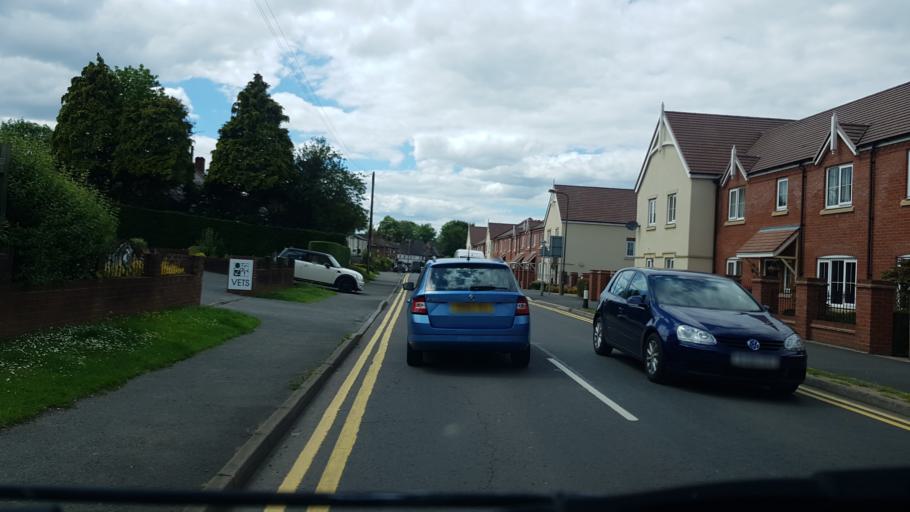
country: GB
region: England
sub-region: Worcestershire
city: Droitwich
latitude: 52.2681
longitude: -2.1400
